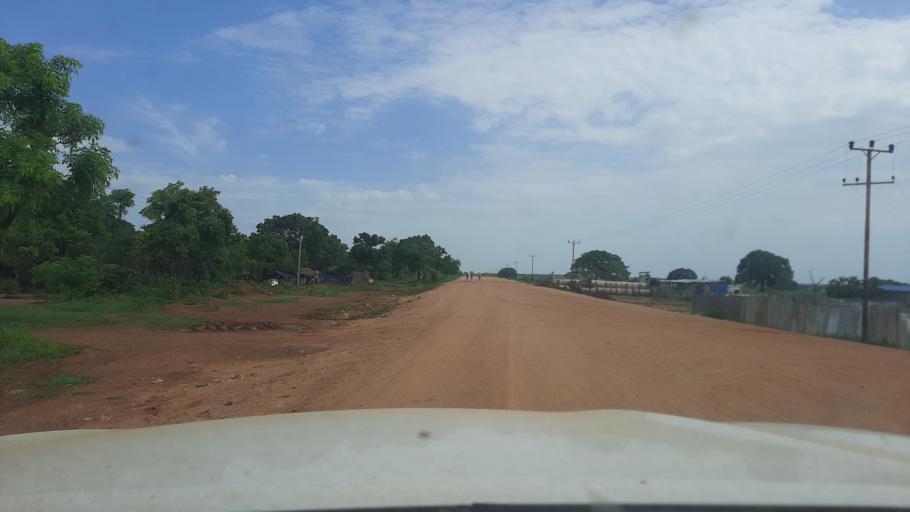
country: ET
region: Gambela
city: Gambela
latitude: 8.0327
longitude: 34.5770
